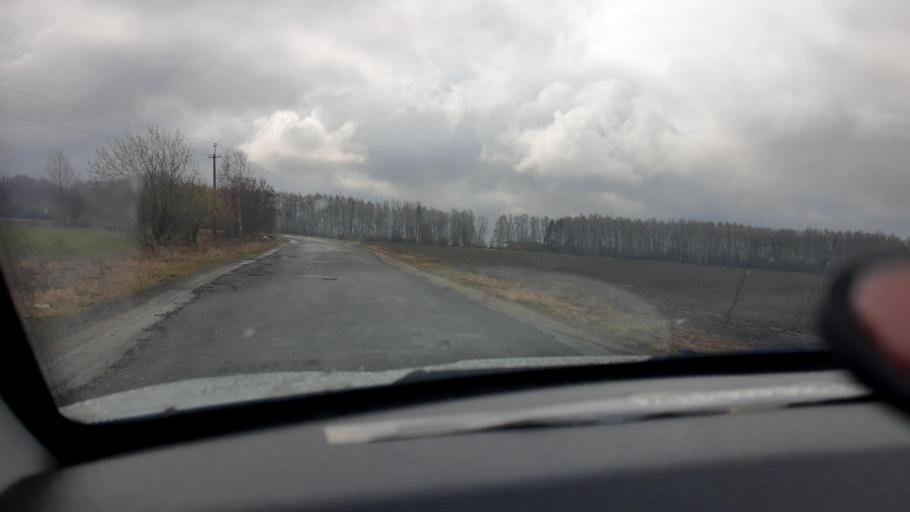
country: RU
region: Nizjnij Novgorod
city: Burevestnik
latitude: 56.1584
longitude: 43.7003
